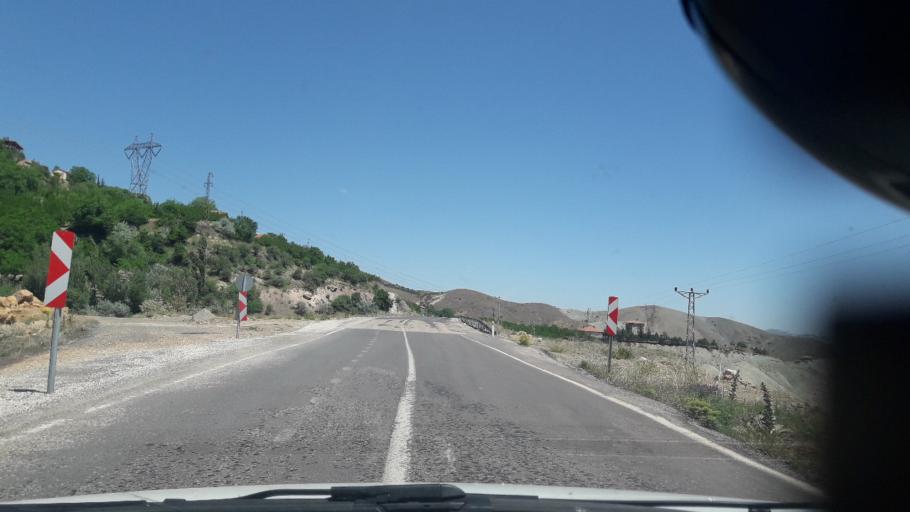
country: TR
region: Malatya
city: Hekimhan
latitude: 38.8403
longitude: 37.8335
